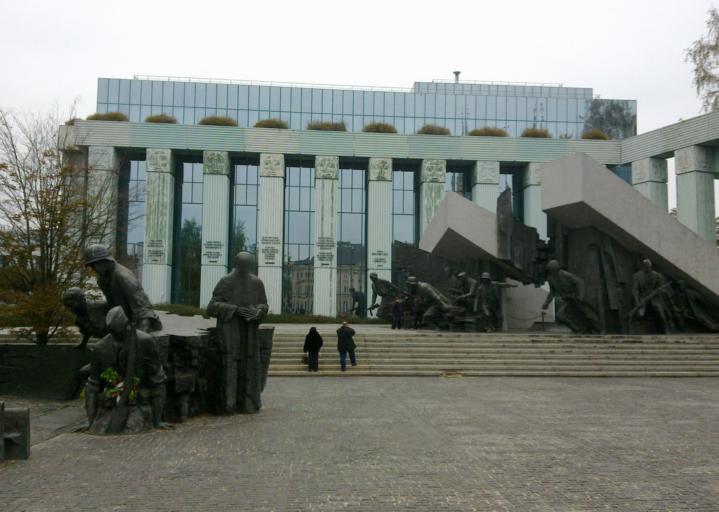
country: PL
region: Masovian Voivodeship
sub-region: Warszawa
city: Wola
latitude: 52.2490
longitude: 21.0061
